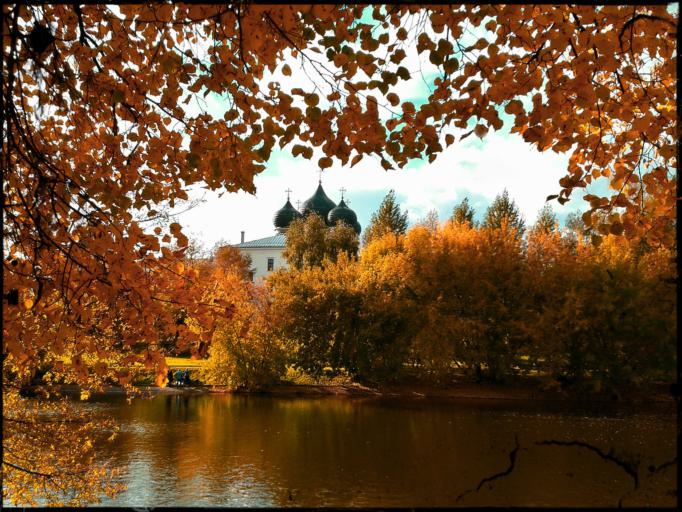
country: RU
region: Moscow
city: Metrogorodok
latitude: 55.7908
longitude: 37.7678
